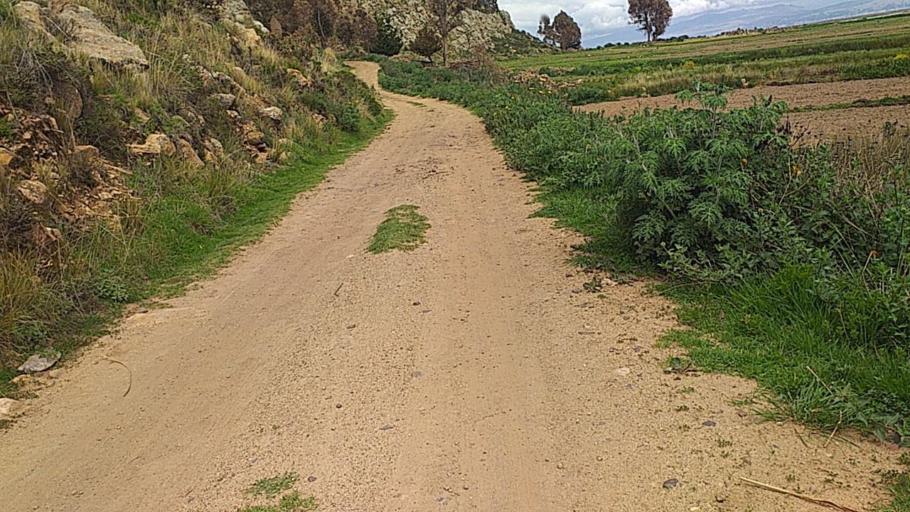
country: BO
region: La Paz
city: Batallas
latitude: -16.3299
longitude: -68.6405
